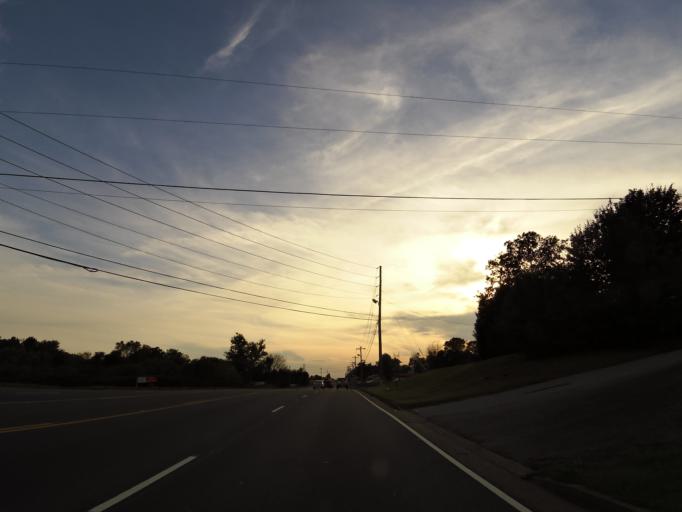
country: US
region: Tennessee
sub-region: Blount County
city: Maryville
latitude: 35.7236
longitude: -84.0021
